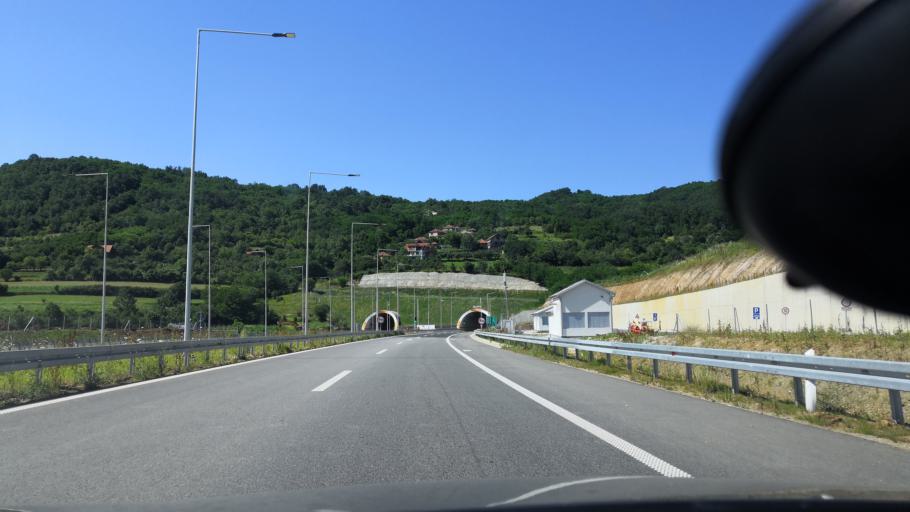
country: RS
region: Central Serbia
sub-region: Pcinjski Okrug
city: Vladicin Han
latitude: 42.7287
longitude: 22.0736
